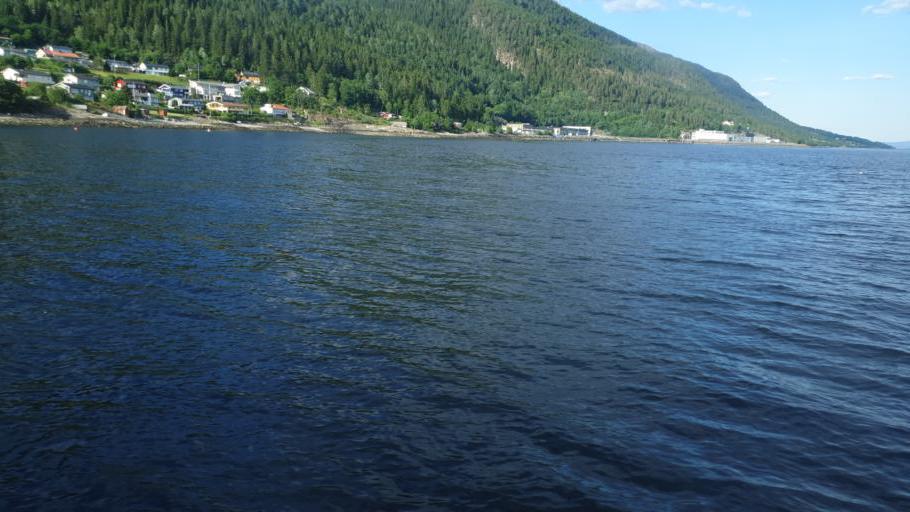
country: NO
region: Sor-Trondelag
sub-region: Trondheim
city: Trondheim
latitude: 63.5530
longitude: 10.2258
